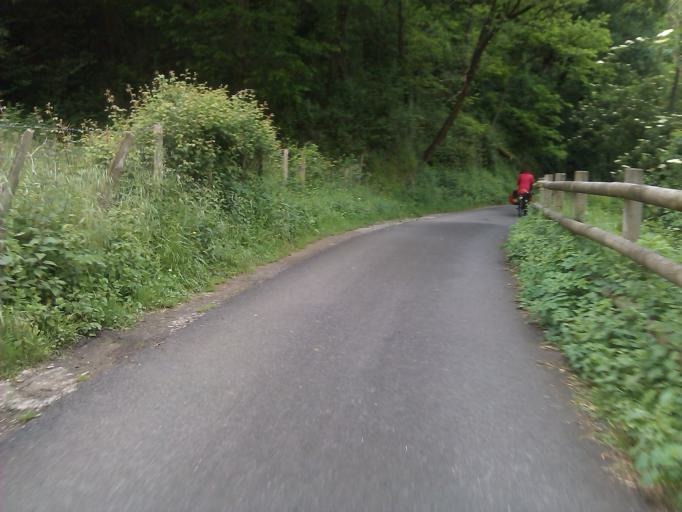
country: ES
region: Basque Country
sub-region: Provincia de Guipuzcoa
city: Andoain
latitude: 43.2130
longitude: -2.0148
